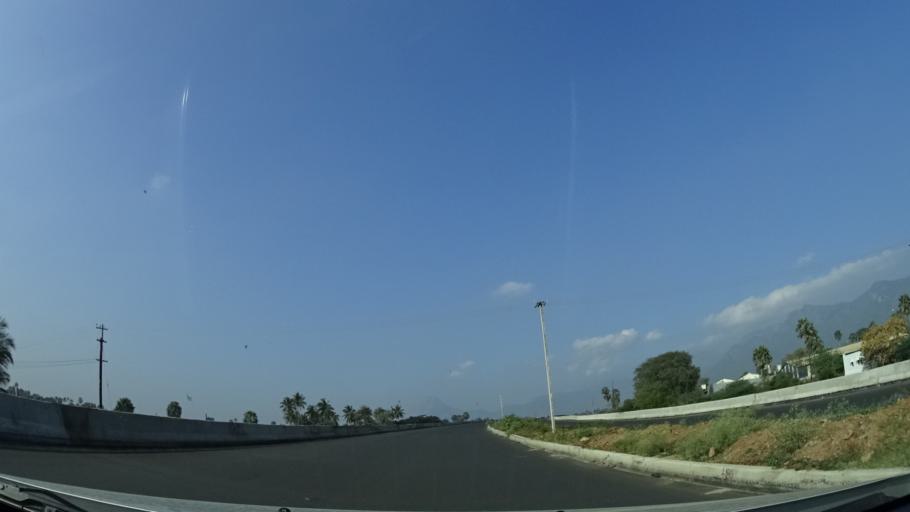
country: IN
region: Tamil Nadu
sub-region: Coimbatore
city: Madukkarai
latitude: 10.8718
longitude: 76.9001
